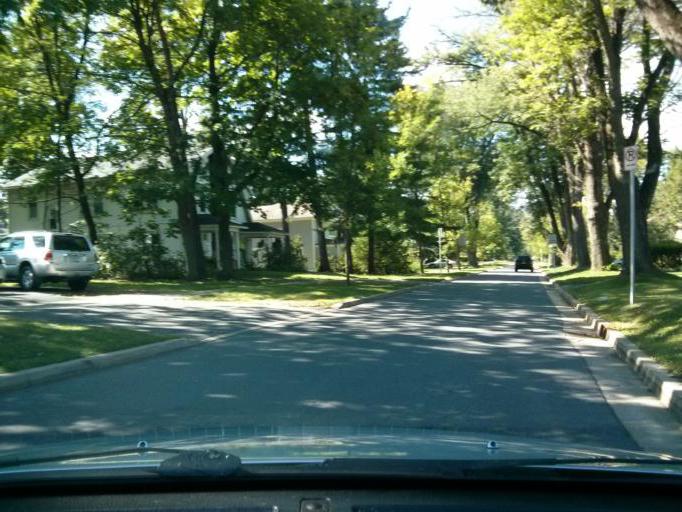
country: US
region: Pennsylvania
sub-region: Centre County
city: State College
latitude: 40.8003
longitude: -77.8711
